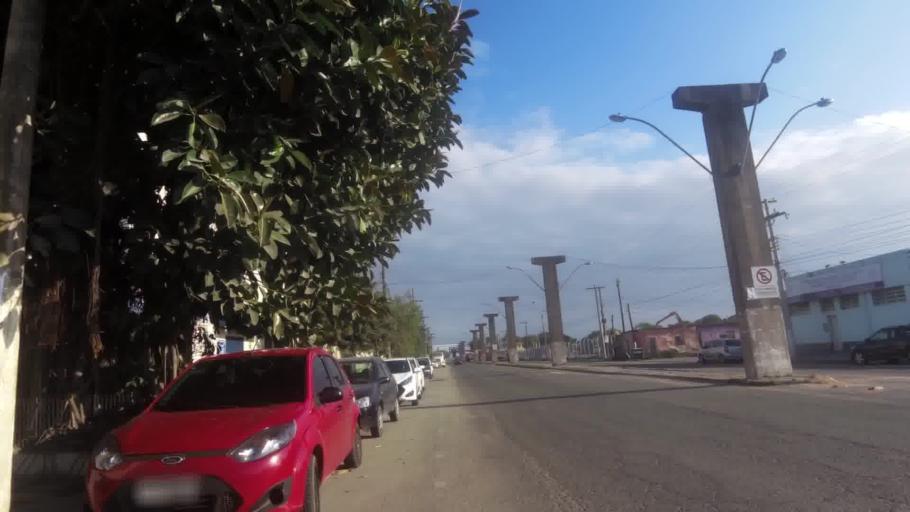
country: BR
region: Rio Grande do Sul
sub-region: Rio Grande
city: Rio Grande
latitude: -32.0427
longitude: -52.0764
